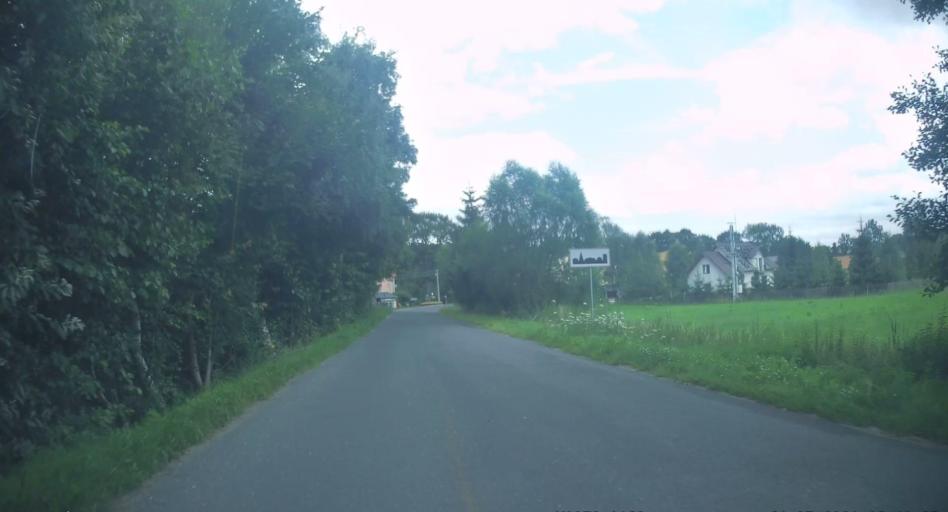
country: PL
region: Lower Silesian Voivodeship
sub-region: Powiat kamiennogorski
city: Marciszow
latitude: 50.8521
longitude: 15.9947
